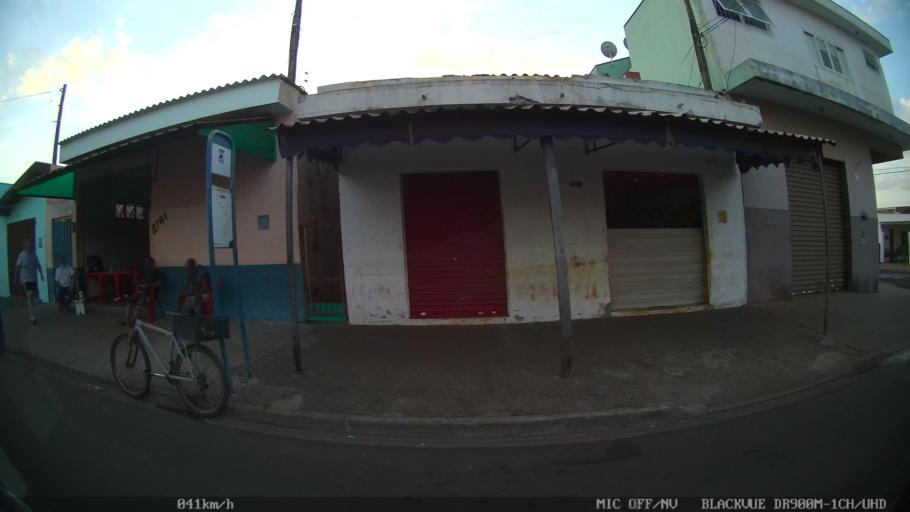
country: BR
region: Sao Paulo
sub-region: Ribeirao Preto
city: Ribeirao Preto
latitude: -21.1386
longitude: -47.8206
